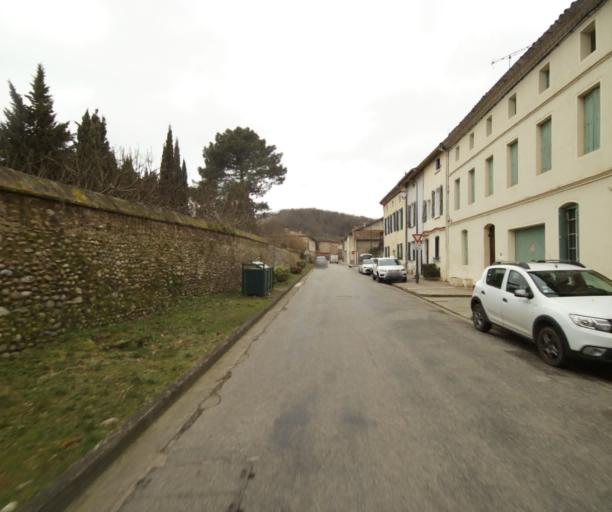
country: FR
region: Midi-Pyrenees
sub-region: Departement de l'Ariege
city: Pamiers
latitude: 43.1649
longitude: 1.5945
